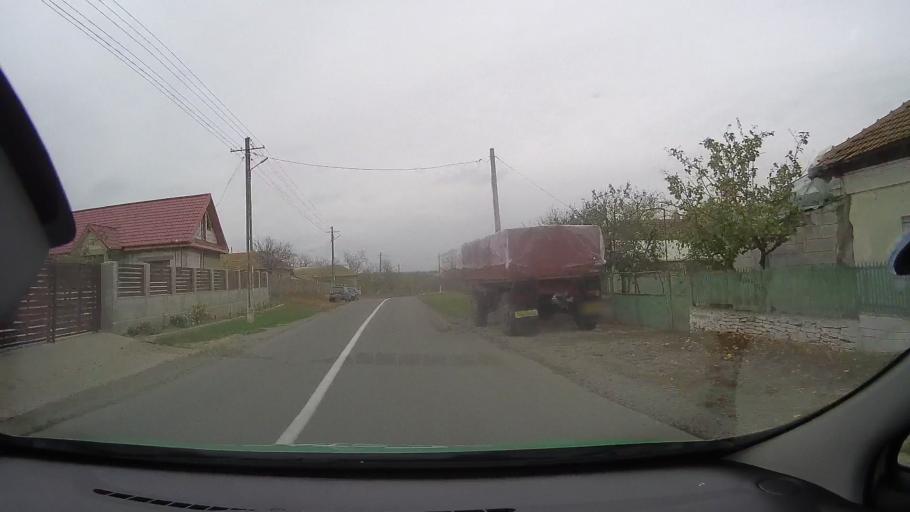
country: RO
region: Constanta
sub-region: Comuna Pantelimon
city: Pantelimon
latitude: 44.4896
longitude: 28.3585
